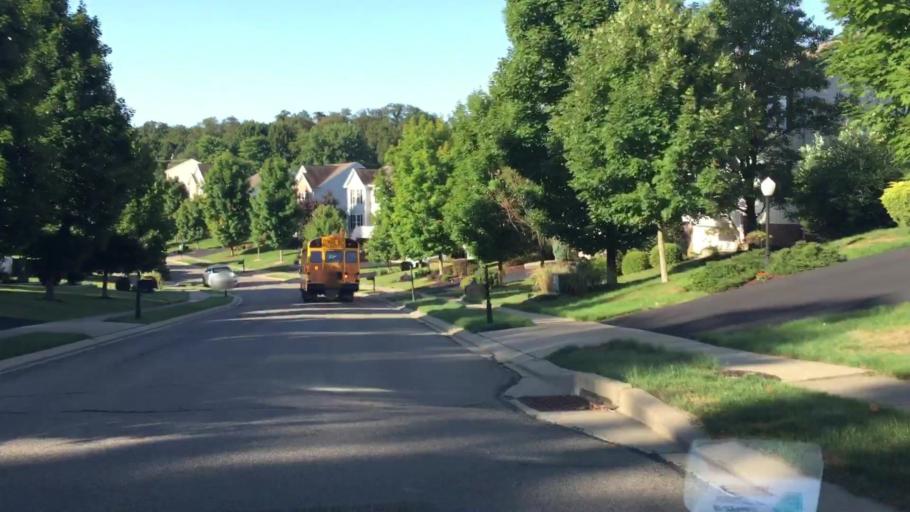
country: US
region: Pennsylvania
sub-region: Allegheny County
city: Franklin Park
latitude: 40.5902
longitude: -80.0963
